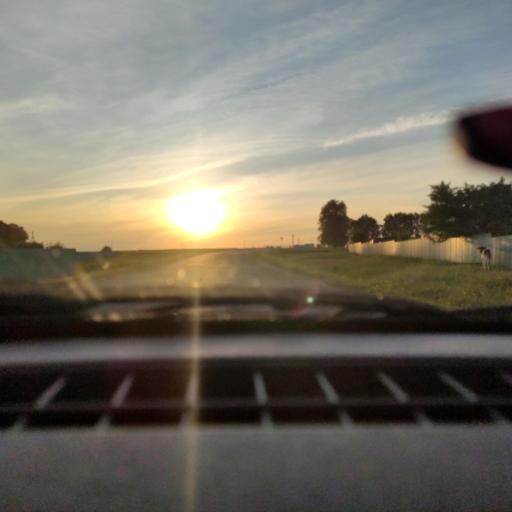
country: RU
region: Bashkortostan
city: Tolbazy
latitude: 54.2942
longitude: 55.8086
